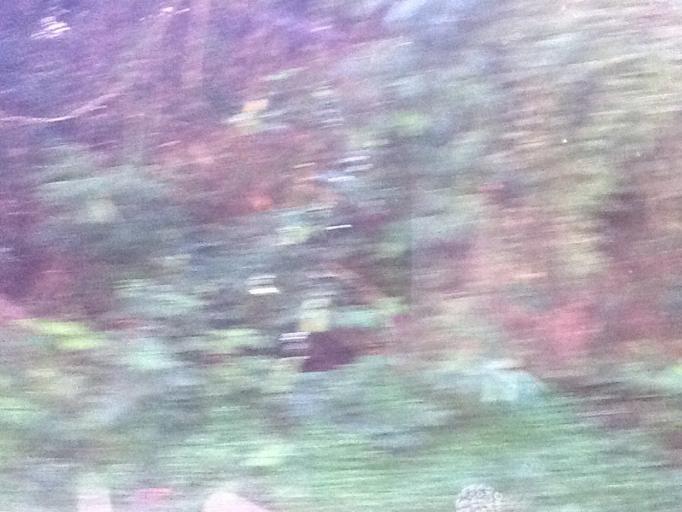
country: TH
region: Phuket
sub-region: Amphoe Kathu
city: Kathu
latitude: 7.9400
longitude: 98.3551
